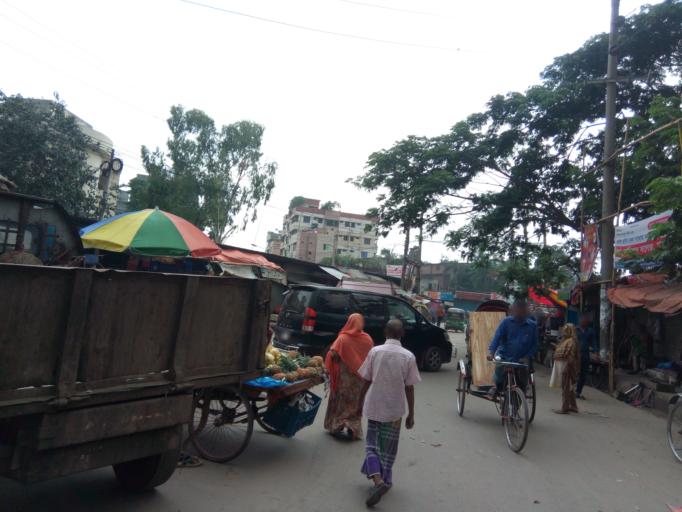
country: BD
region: Dhaka
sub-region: Dhaka
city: Dhaka
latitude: 23.7179
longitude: 90.4313
